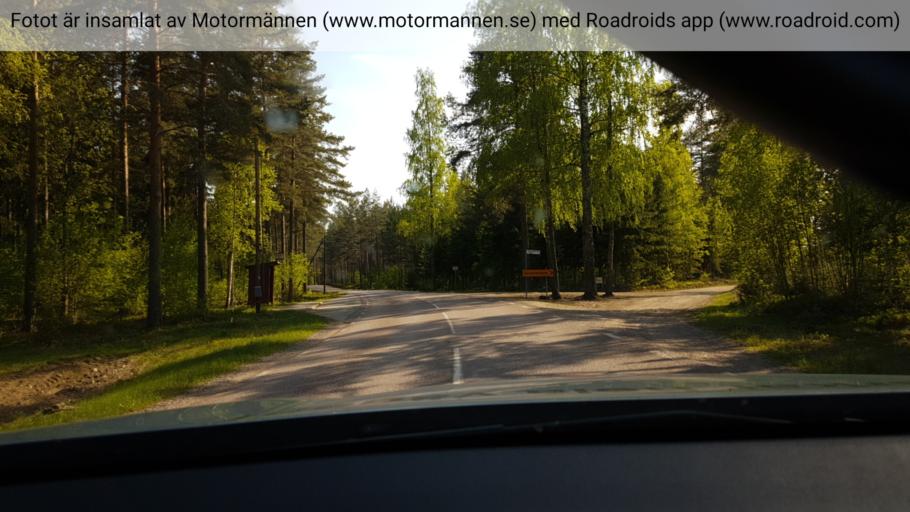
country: SE
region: Gaevleborg
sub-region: Sandvikens Kommun
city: Arsunda
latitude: 60.4499
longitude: 16.6941
